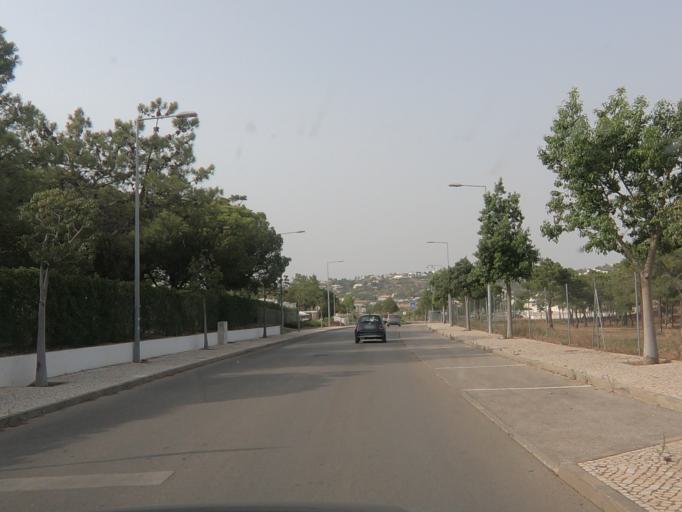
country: PT
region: Faro
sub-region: Albufeira
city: Albufeira
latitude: 37.0802
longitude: -8.2987
